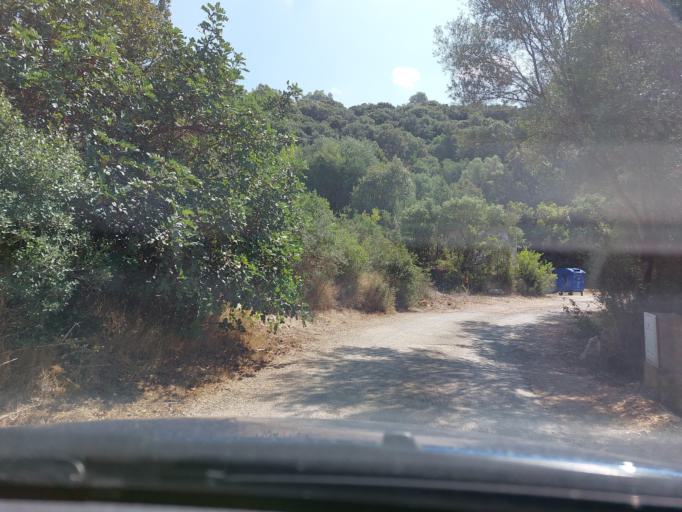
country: HR
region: Dubrovacko-Neretvanska
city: Smokvica
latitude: 42.7721
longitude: 16.8397
